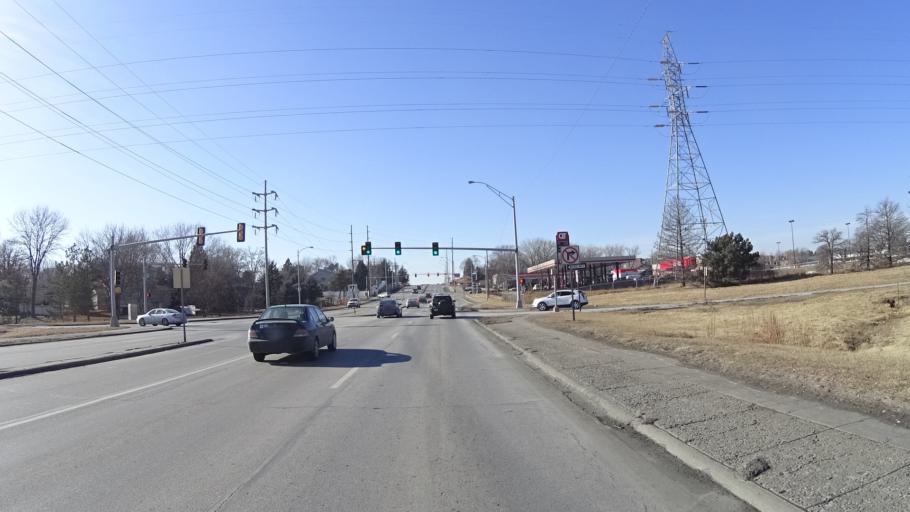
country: US
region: Nebraska
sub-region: Douglas County
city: Bennington
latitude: 41.3067
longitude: -96.0715
